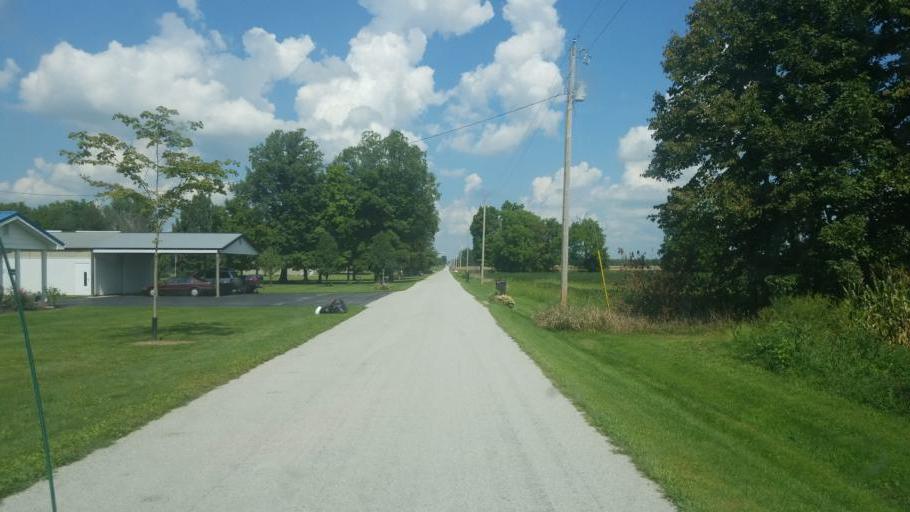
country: US
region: Ohio
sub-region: Hardin County
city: Ada
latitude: 40.7441
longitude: -83.7097
